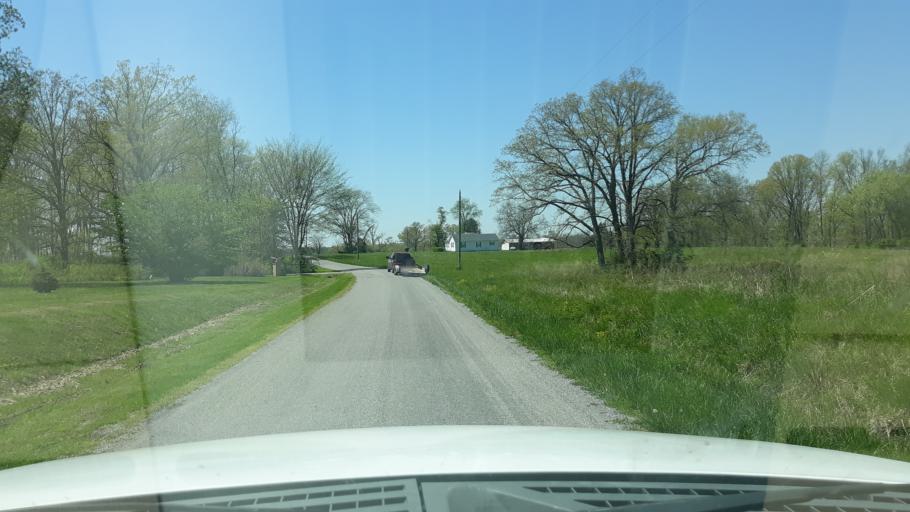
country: US
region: Illinois
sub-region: Saline County
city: Harrisburg
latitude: 37.8848
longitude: -88.6629
